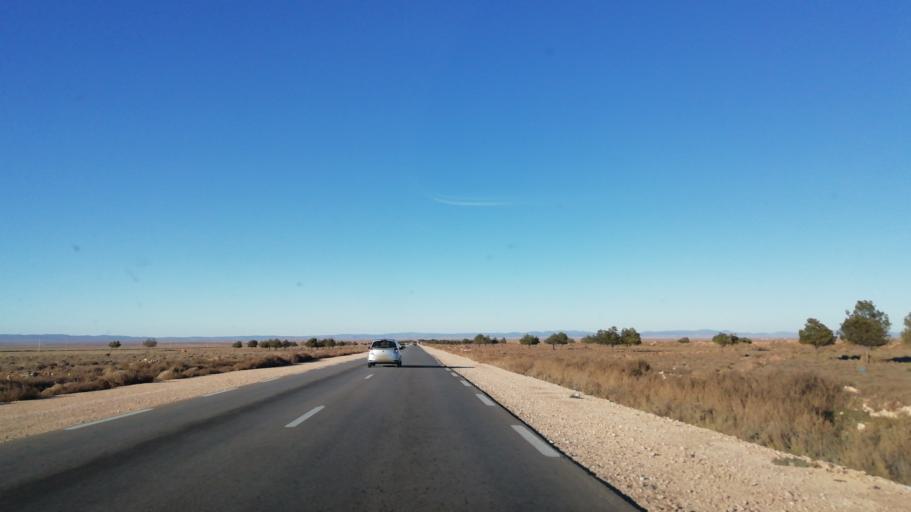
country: DZ
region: Tlemcen
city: Sebdou
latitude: 34.3271
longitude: -1.2639
